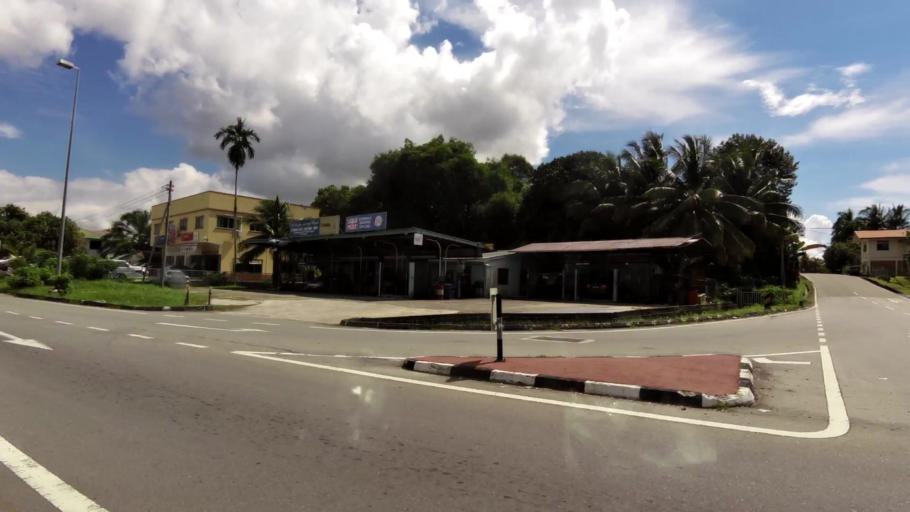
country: BN
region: Brunei and Muara
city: Bandar Seri Begawan
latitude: 4.9707
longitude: 114.9456
